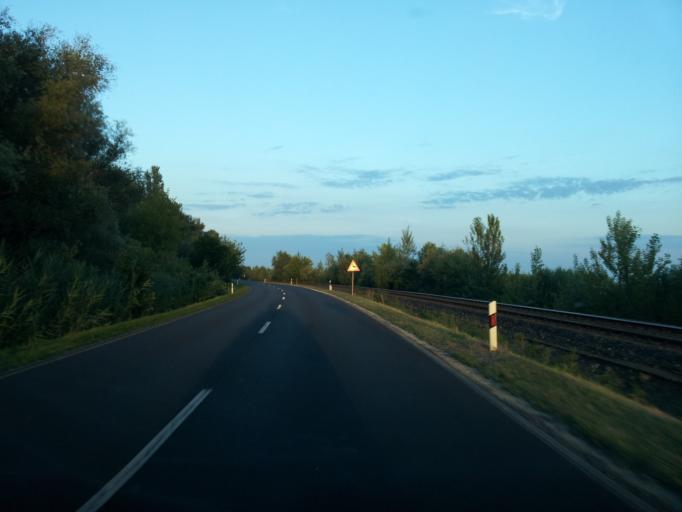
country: HU
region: Veszprem
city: Balatonalmadi
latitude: 47.0423
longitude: 18.0633
